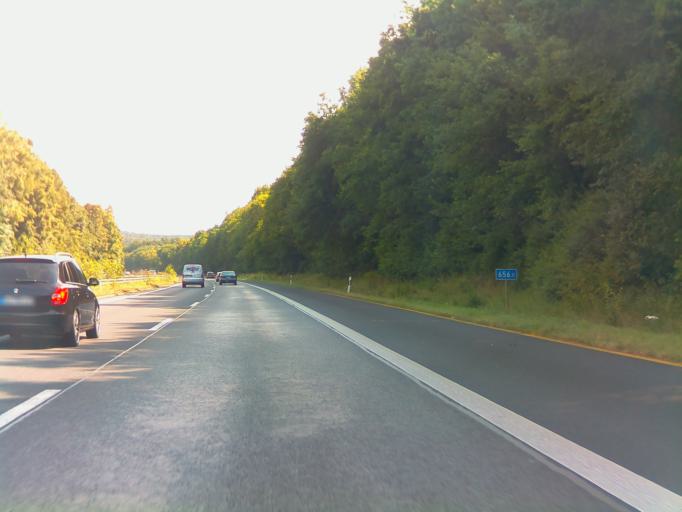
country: DE
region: Bavaria
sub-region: Regierungsbezirk Unterfranken
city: Rimpar
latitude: 49.8735
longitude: 9.9922
